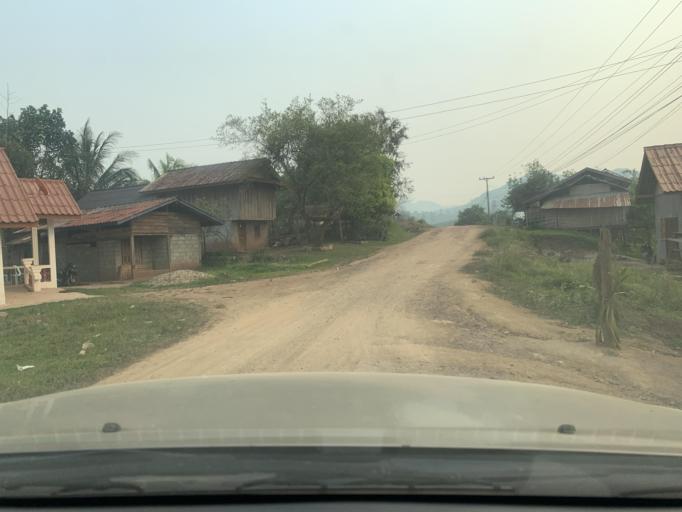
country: LA
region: Louangphabang
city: Louangphabang
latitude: 19.9184
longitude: 102.0751
